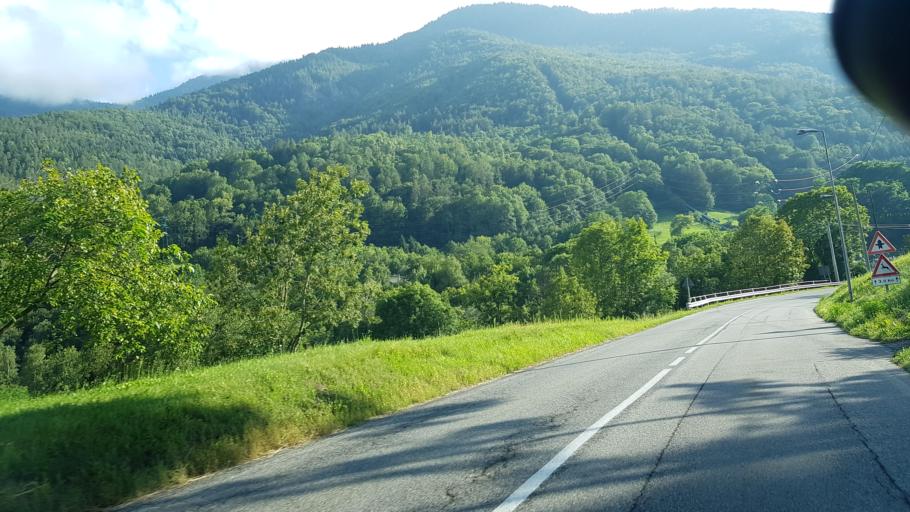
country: IT
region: Piedmont
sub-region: Provincia di Cuneo
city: Sampeyre
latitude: 44.5762
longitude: 7.1977
